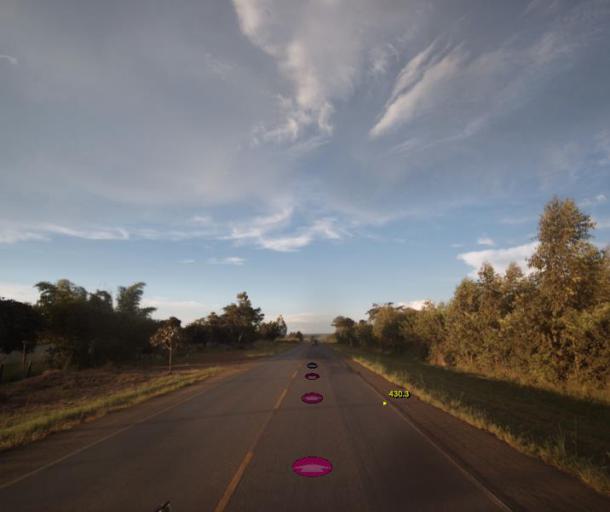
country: BR
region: Goias
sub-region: Anapolis
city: Anapolis
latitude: -16.2089
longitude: -48.9152
